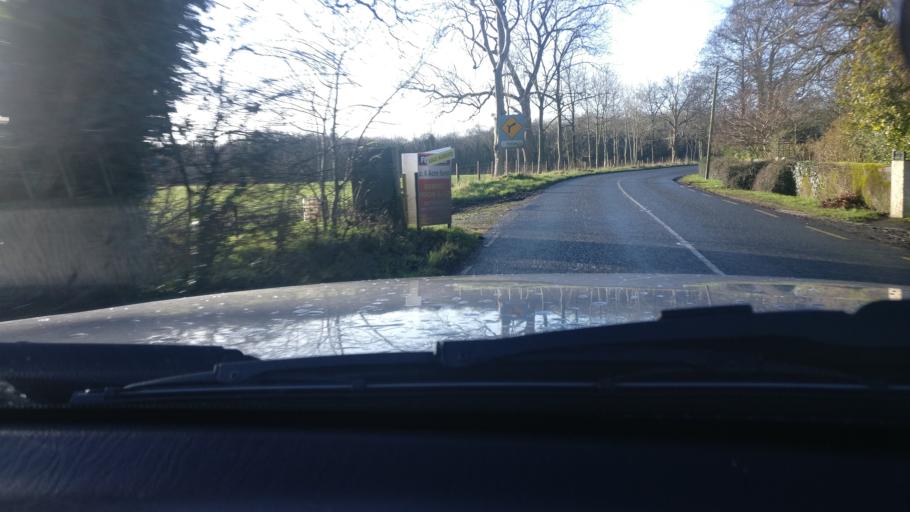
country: IE
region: Ulster
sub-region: An Cabhan
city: Ballyjamesduff
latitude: 53.8194
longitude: -7.3457
